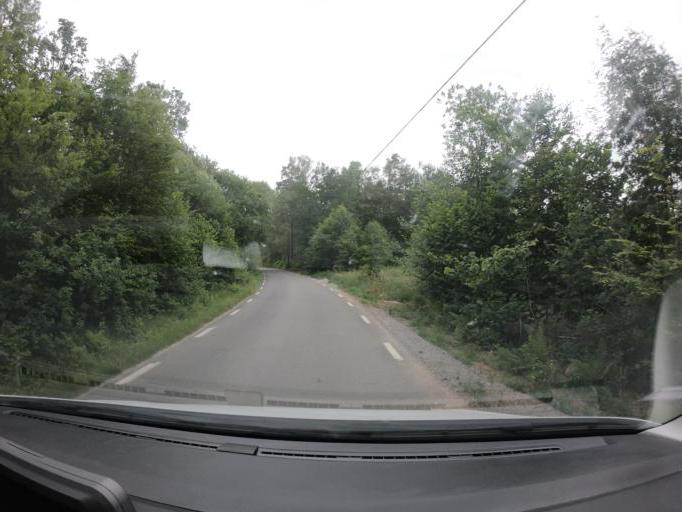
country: SE
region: Skane
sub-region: Hassleholms Kommun
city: Tormestorp
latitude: 56.1218
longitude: 13.6490
